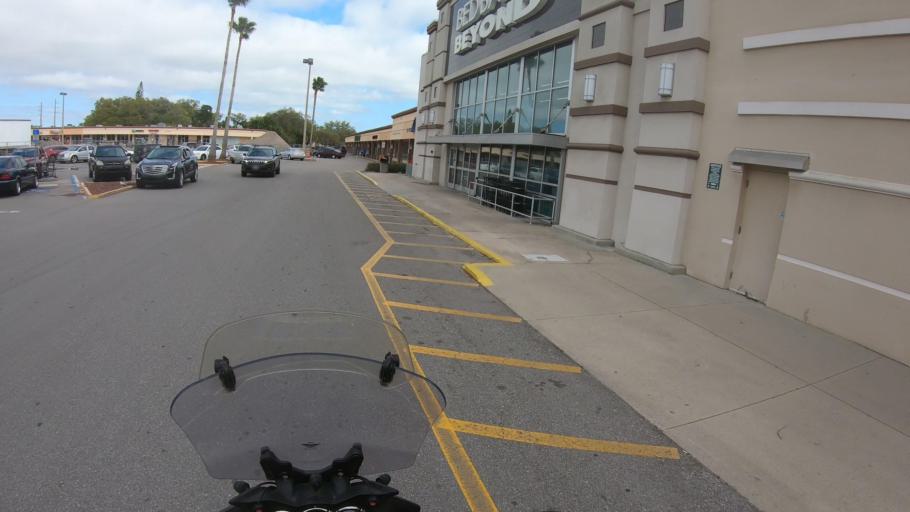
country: US
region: Florida
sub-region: Manatee County
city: South Bradenton
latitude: 27.4609
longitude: -82.5698
